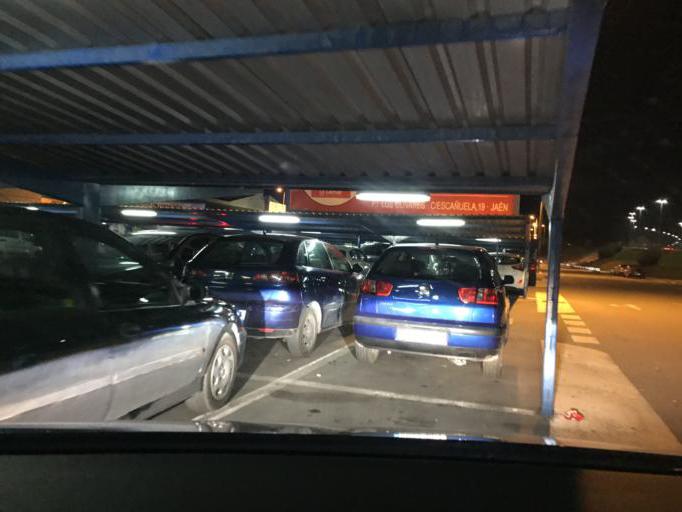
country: ES
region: Andalusia
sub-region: Provincia de Jaen
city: Jaen
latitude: 37.7816
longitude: -3.7652
